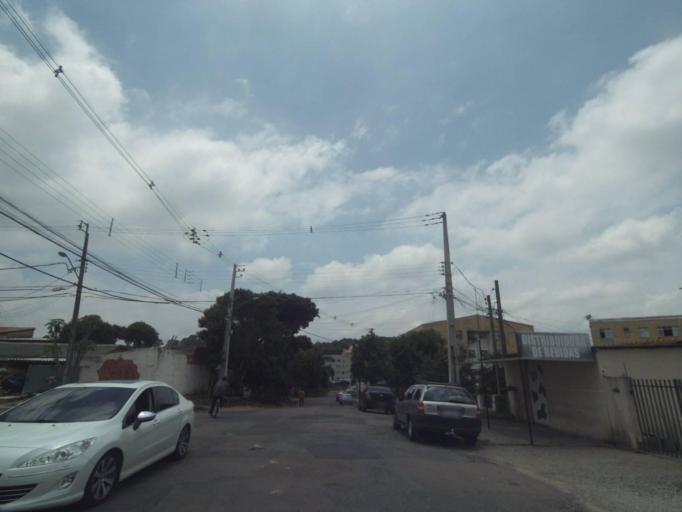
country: BR
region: Parana
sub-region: Curitiba
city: Curitiba
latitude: -25.4769
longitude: -49.3337
